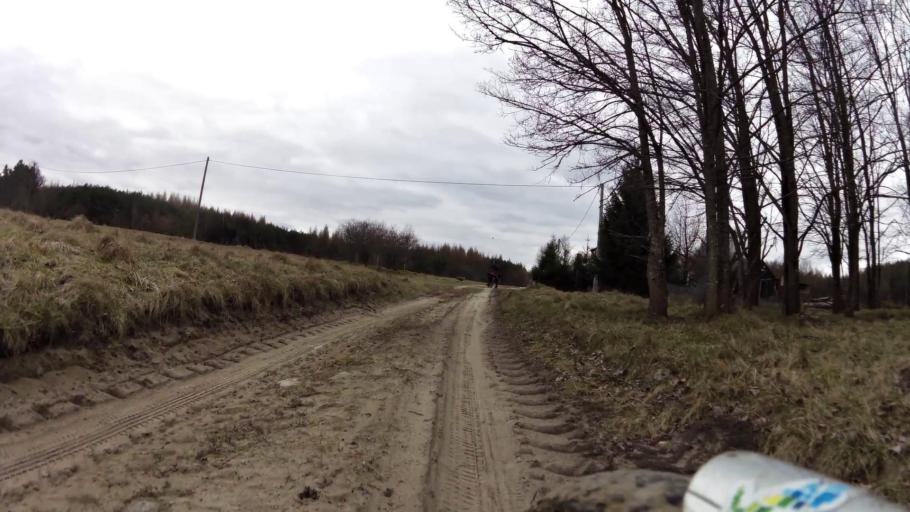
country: PL
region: Pomeranian Voivodeship
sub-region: Powiat bytowski
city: Trzebielino
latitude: 54.1201
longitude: 17.1293
